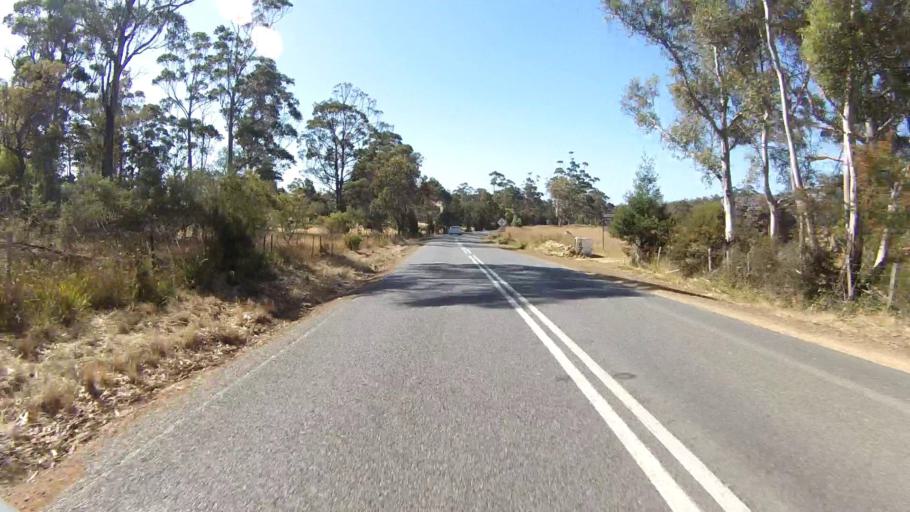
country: AU
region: Tasmania
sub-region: Sorell
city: Sorell
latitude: -42.3216
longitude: 147.9538
